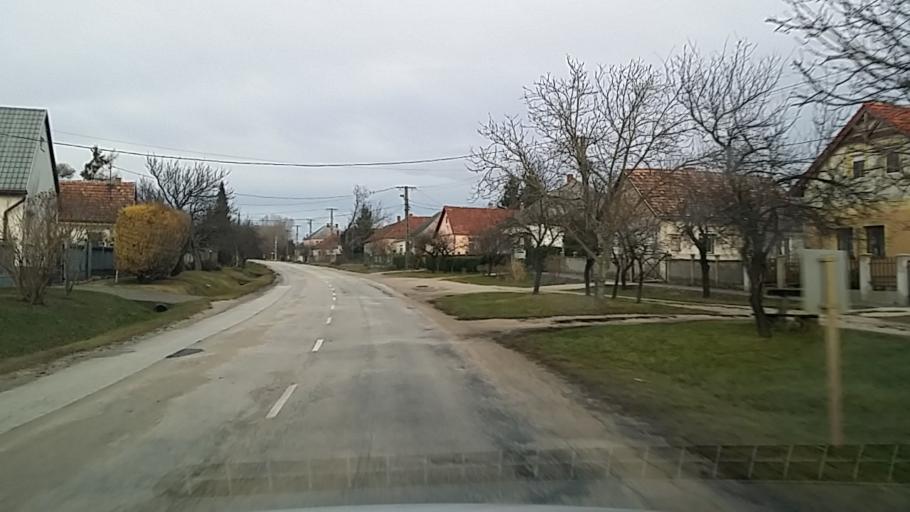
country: HU
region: Fejer
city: Fehervarcsurgo
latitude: 47.3214
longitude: 18.2818
